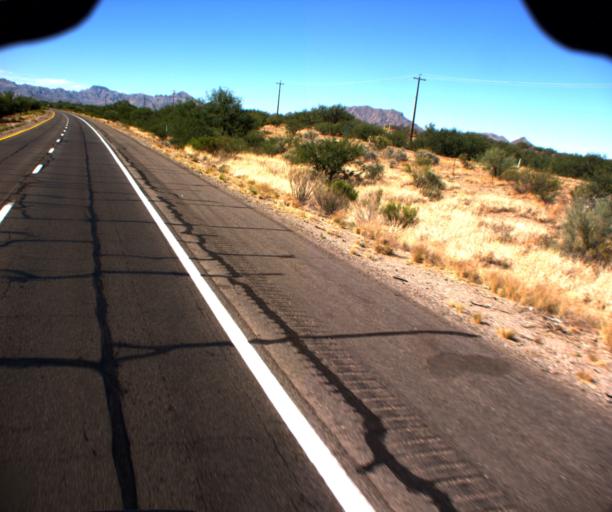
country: US
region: Arizona
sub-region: Pima County
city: Arivaca Junction
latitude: 31.7134
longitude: -111.0641
